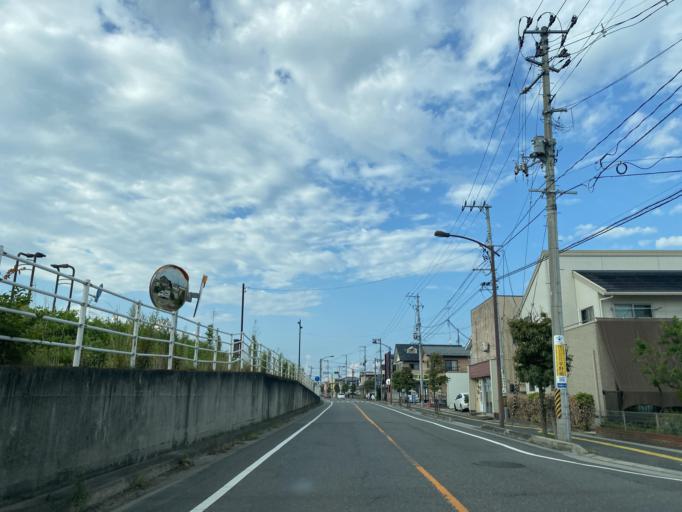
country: JP
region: Fukushima
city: Koriyama
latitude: 37.3640
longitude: 140.3839
